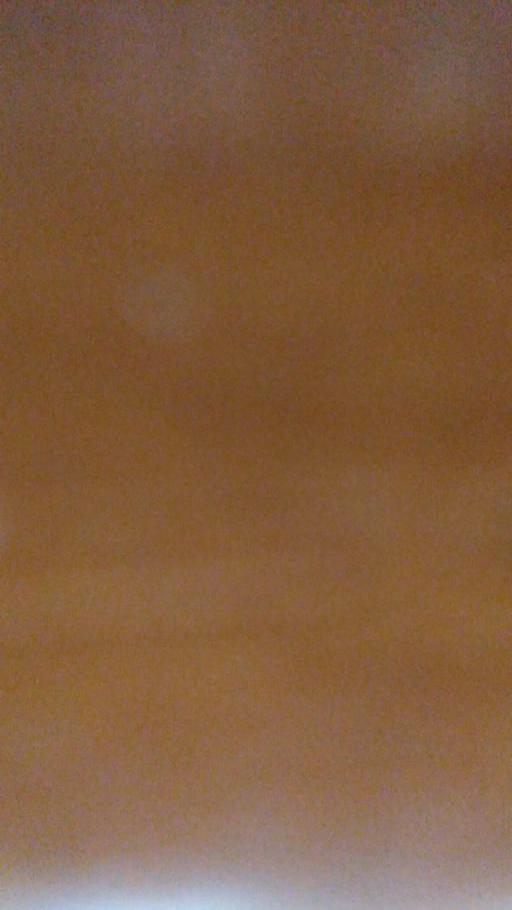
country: RU
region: Tula
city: Kazachka
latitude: 53.4878
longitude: 38.1166
